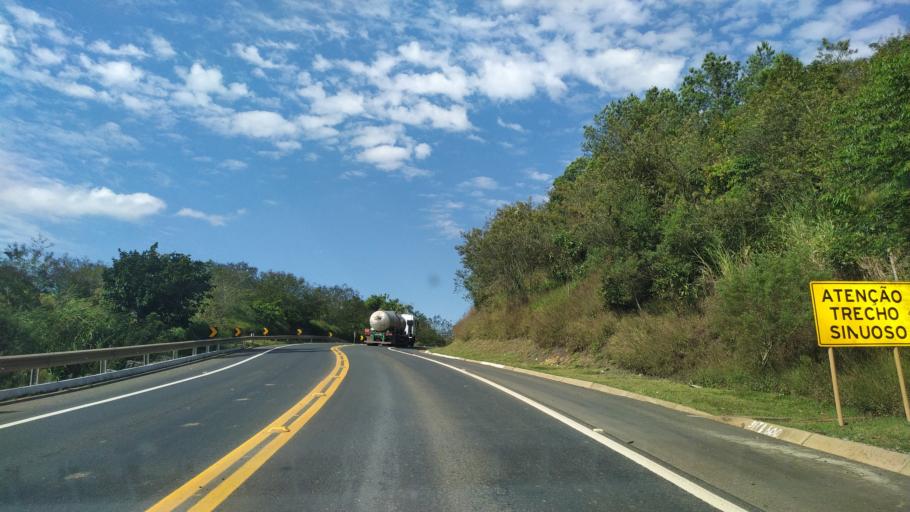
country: BR
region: Parana
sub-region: Telemaco Borba
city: Telemaco Borba
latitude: -24.2700
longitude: -50.7185
